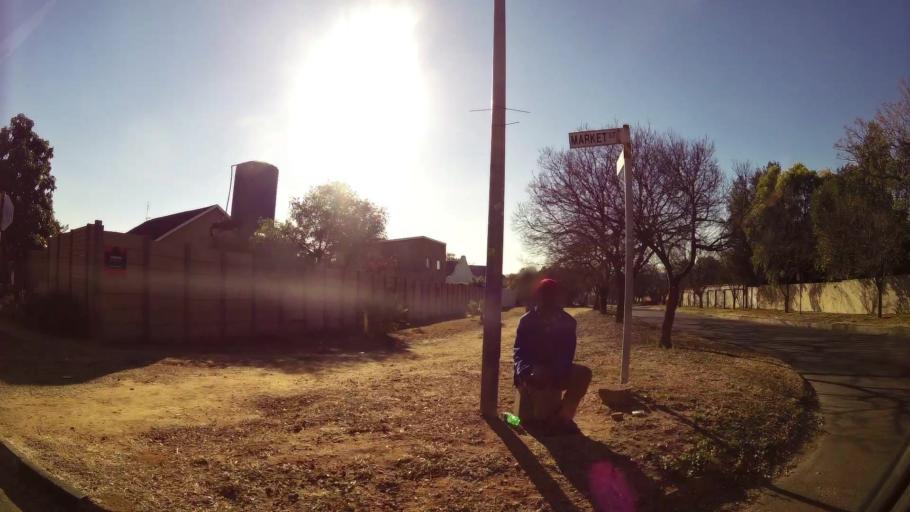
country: ZA
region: Gauteng
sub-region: City of Johannesburg Metropolitan Municipality
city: Diepsloot
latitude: -26.0531
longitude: 27.9771
